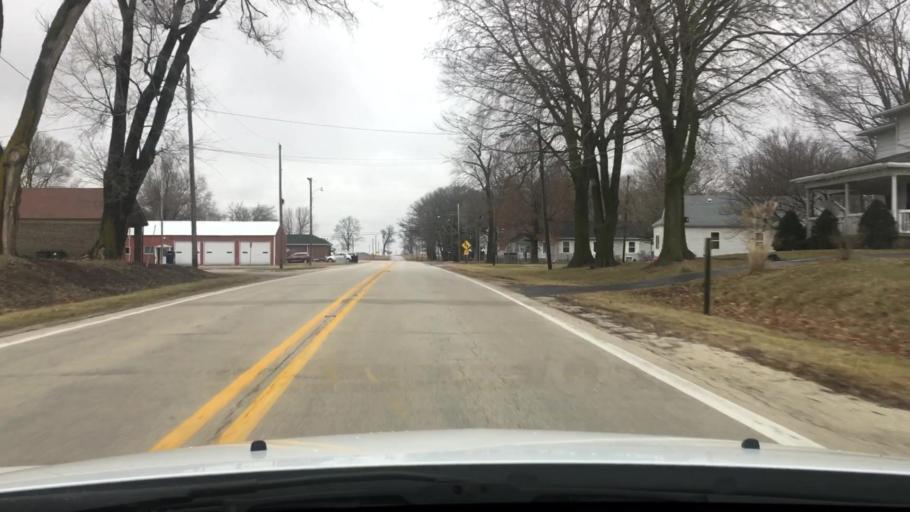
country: US
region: Illinois
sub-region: Iroquois County
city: Sheldon
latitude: 40.8258
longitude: -87.5816
